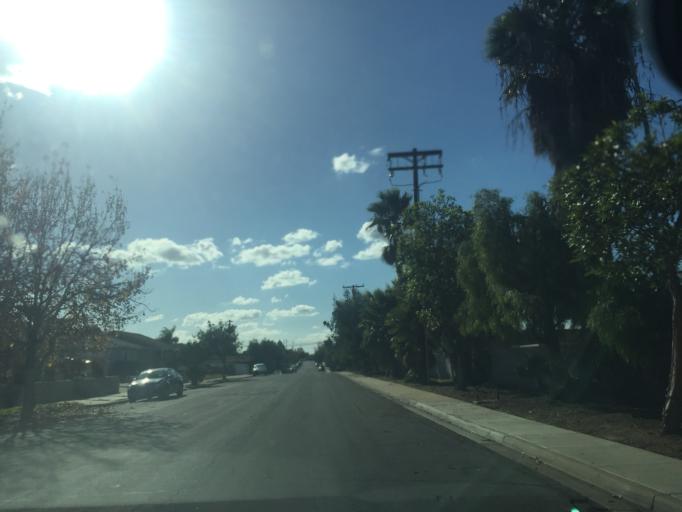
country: US
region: California
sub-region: San Diego County
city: La Mesa
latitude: 32.7914
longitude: -117.0798
